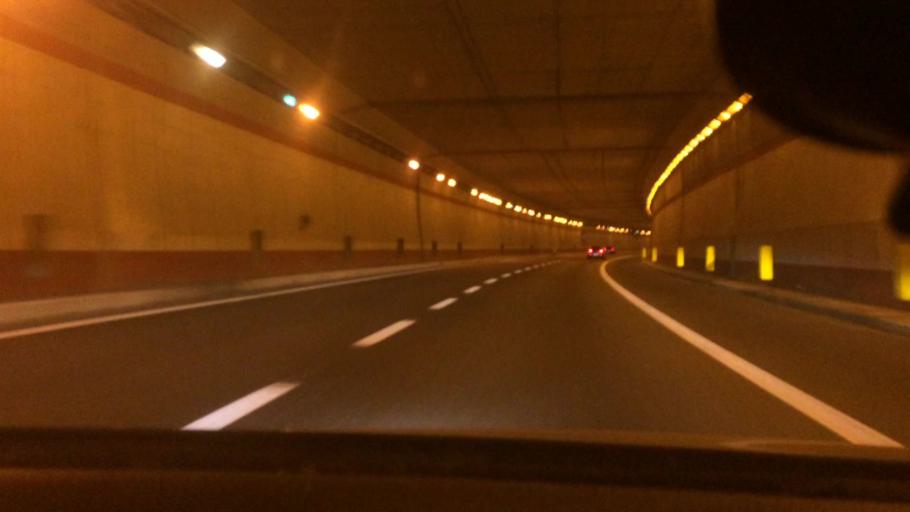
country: IT
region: Lombardy
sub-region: Citta metropolitana di Milano
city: Vanzaghello
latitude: 45.5728
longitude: 8.7715
